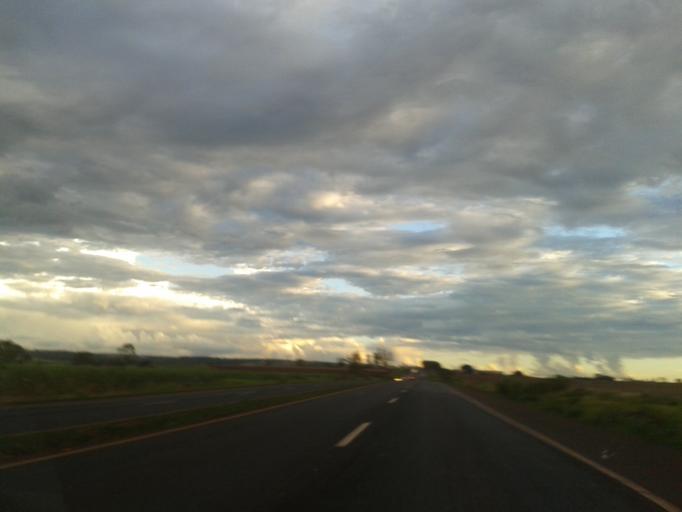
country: BR
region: Minas Gerais
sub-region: Centralina
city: Centralina
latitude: -18.5562
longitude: -49.1939
